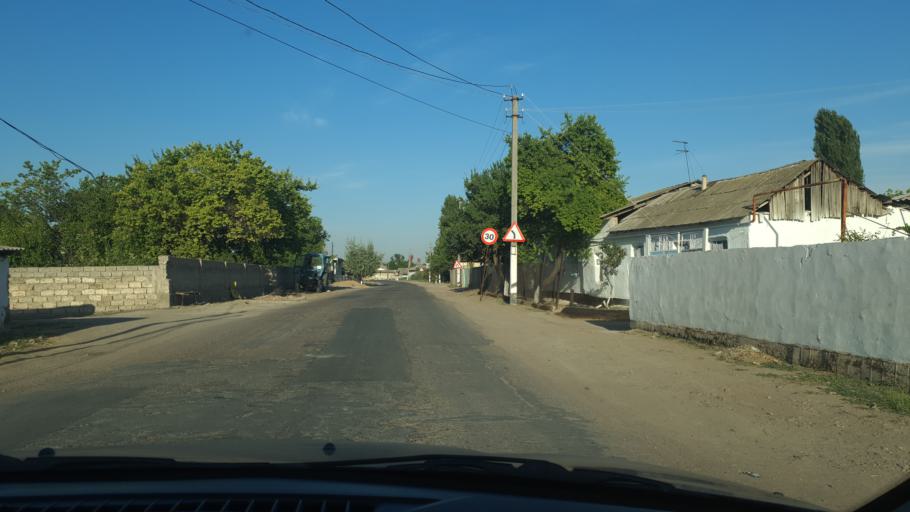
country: UZ
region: Toshkent
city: Tuytepa
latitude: 41.0844
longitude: 69.3300
